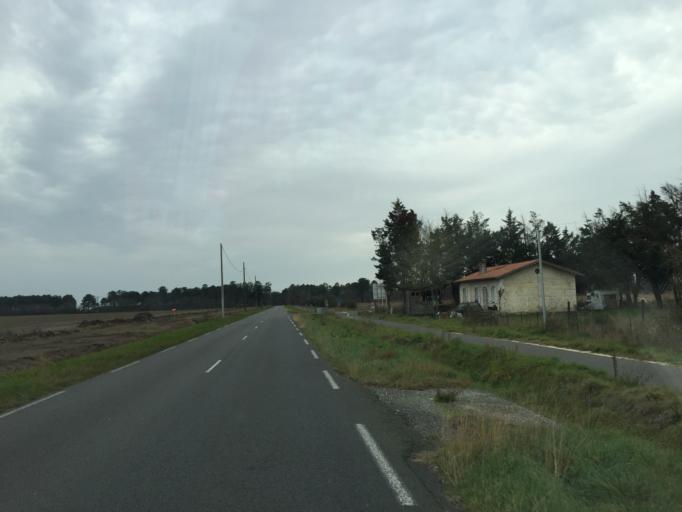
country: FR
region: Aquitaine
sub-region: Departement de la Gironde
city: Carcans
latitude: 45.0506
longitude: -1.0555
